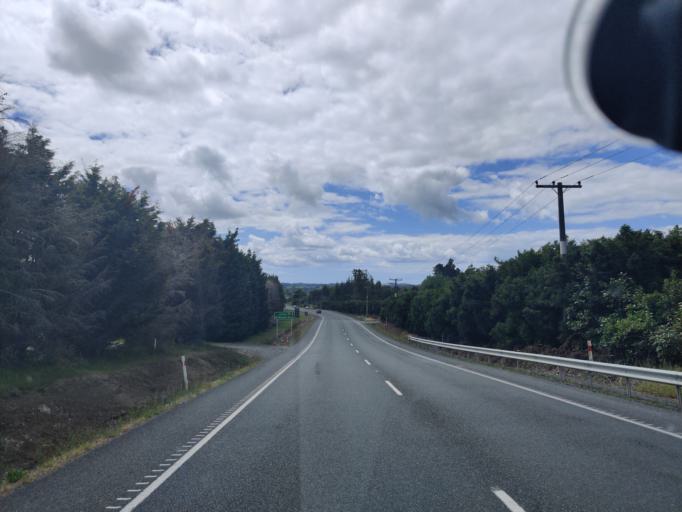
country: NZ
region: Northland
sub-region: Far North District
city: Kerikeri
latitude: -35.2382
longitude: 173.9185
